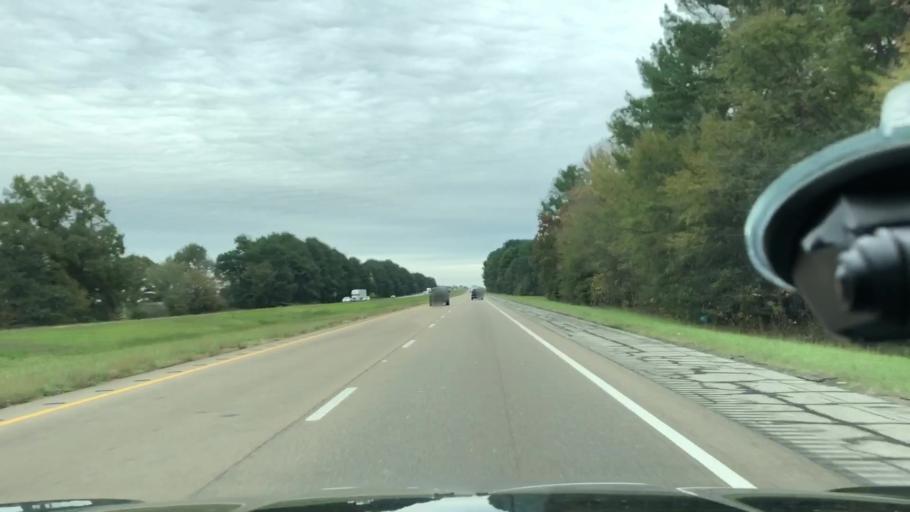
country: US
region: Texas
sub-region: Morris County
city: Omaha
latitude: 33.2795
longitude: -94.7995
